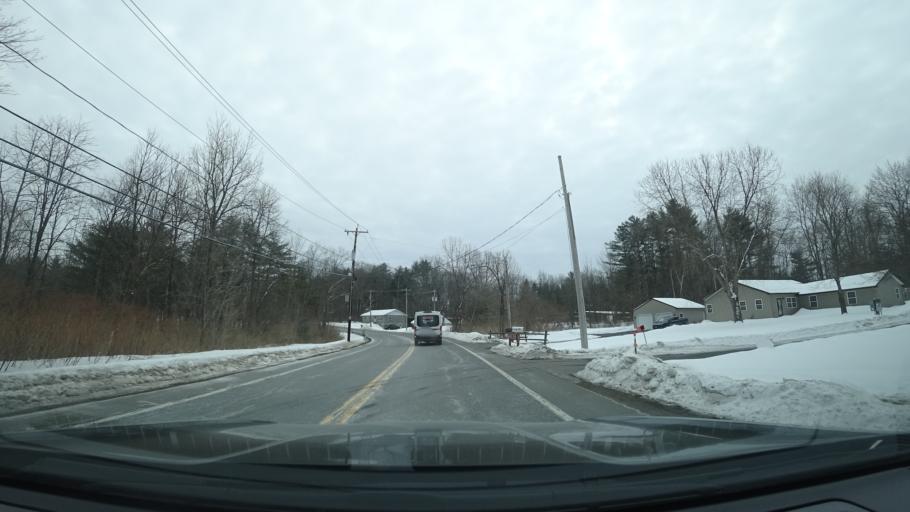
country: US
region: New York
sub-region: Washington County
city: Fort Edward
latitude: 43.2614
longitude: -73.6055
